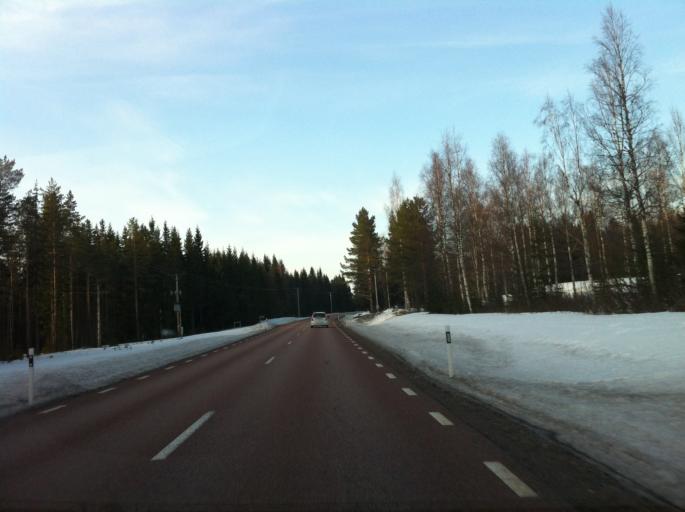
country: SE
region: Dalarna
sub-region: Vansbro Kommun
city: Vansbro
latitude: 60.2679
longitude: 14.1722
